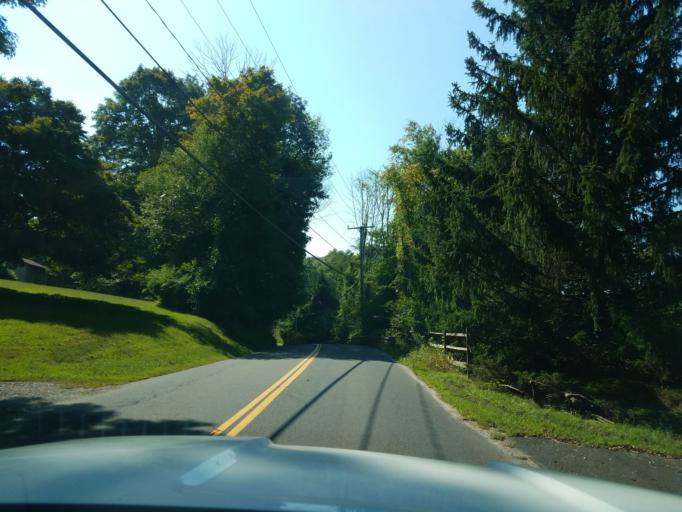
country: US
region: Connecticut
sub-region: Fairfield County
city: Newtown
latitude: 41.3642
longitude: -73.3377
